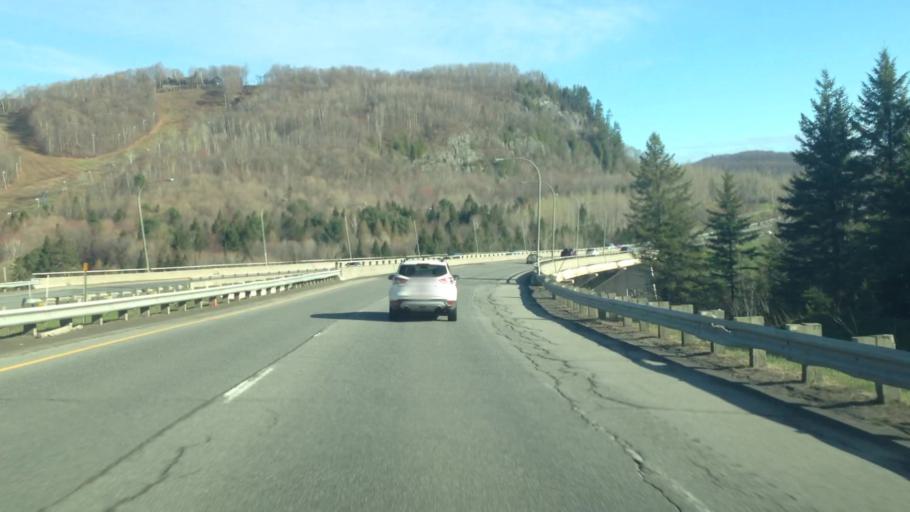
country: CA
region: Quebec
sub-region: Laurentides
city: Saint-Sauveur
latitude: 45.9121
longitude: -74.1501
